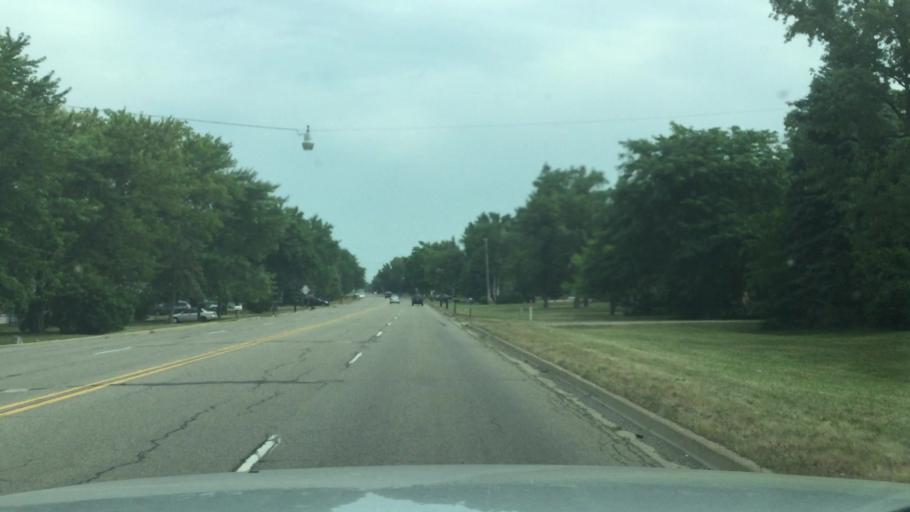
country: US
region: Michigan
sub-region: Genesee County
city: Flint
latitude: 42.9606
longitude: -83.7125
